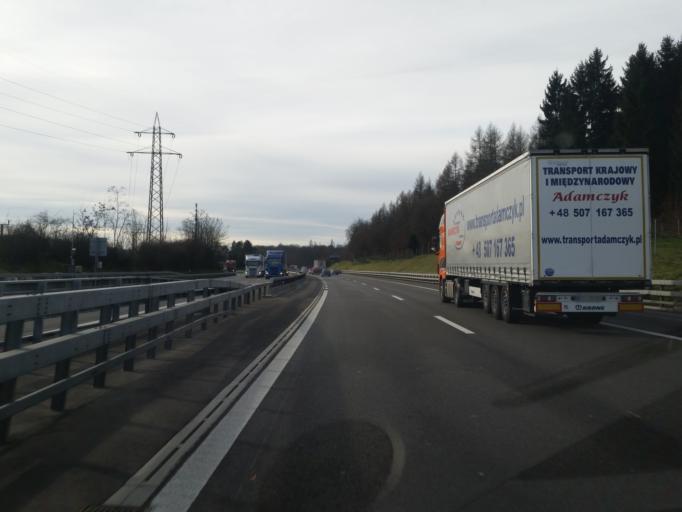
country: CH
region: Aargau
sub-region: Bezirk Lenzburg
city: Othmarsingen
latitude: 47.4048
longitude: 8.2095
